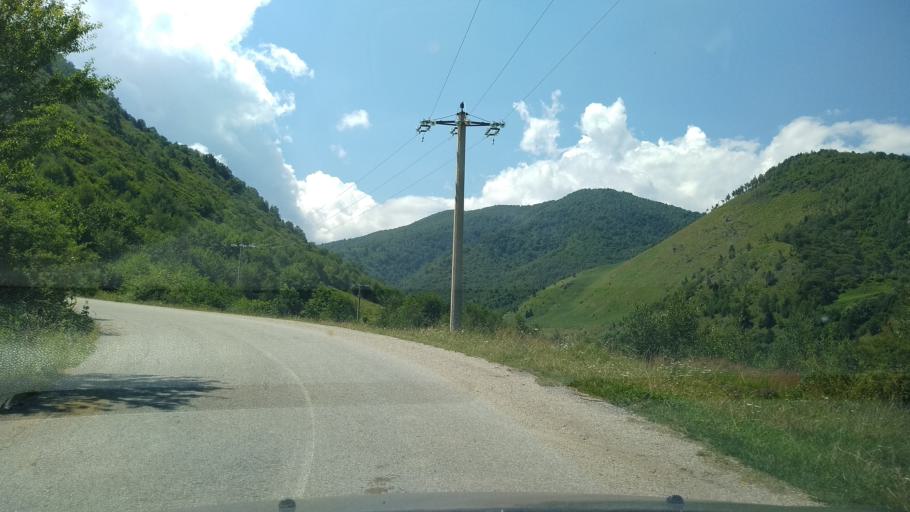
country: RO
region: Hunedoara
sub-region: Comuna Rau de Mori
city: Rau de Mori
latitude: 45.4738
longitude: 22.9062
